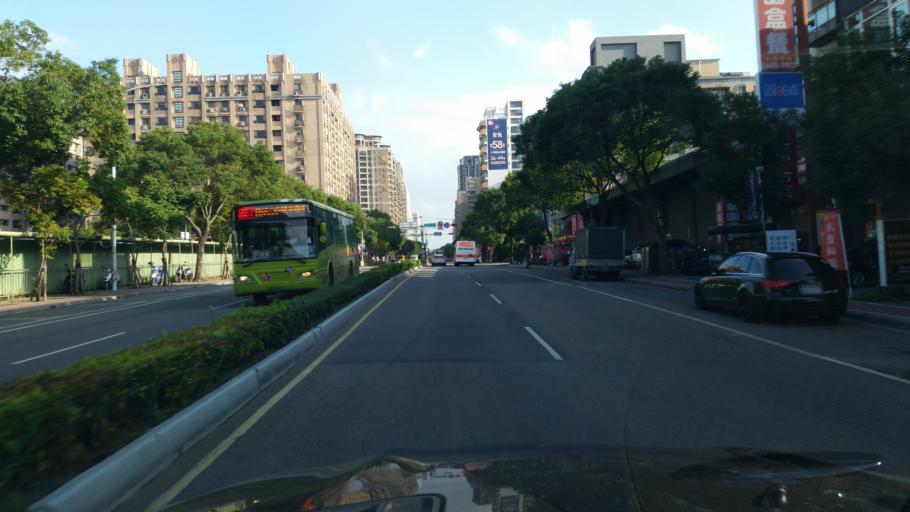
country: TW
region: Taiwan
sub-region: Taoyuan
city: Taoyuan
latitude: 25.0803
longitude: 121.3698
